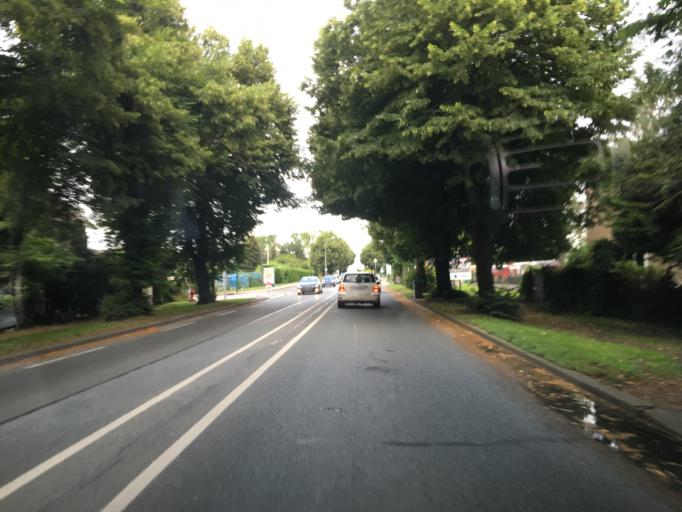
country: FR
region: Ile-de-France
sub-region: Departement du Val-de-Marne
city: Santeny
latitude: 48.7170
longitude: 2.5713
